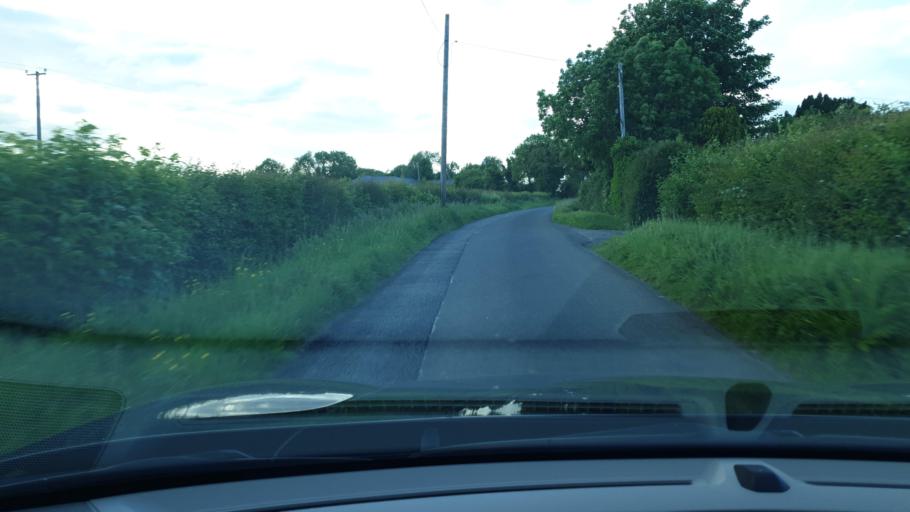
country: IE
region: Leinster
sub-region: An Mhi
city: Ashbourne
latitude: 53.5221
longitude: -6.3868
